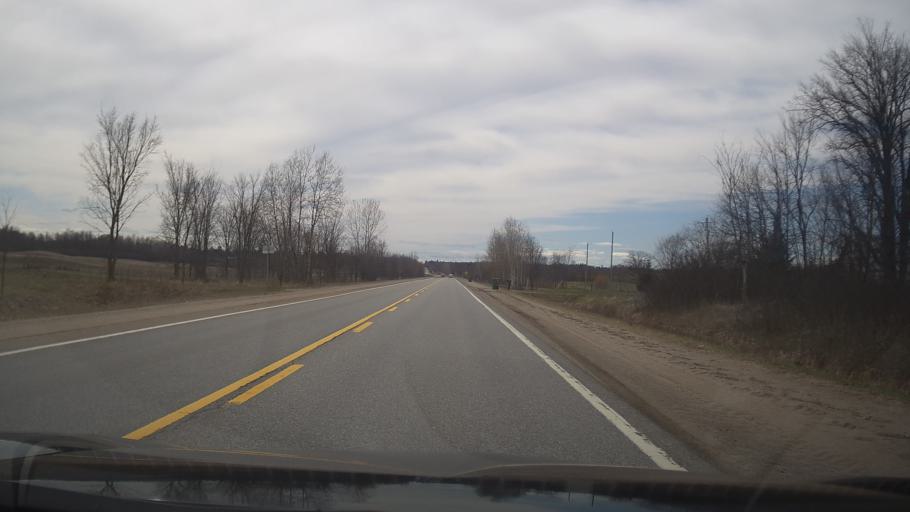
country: CA
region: Ontario
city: Arnprior
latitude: 45.5265
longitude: -76.2570
